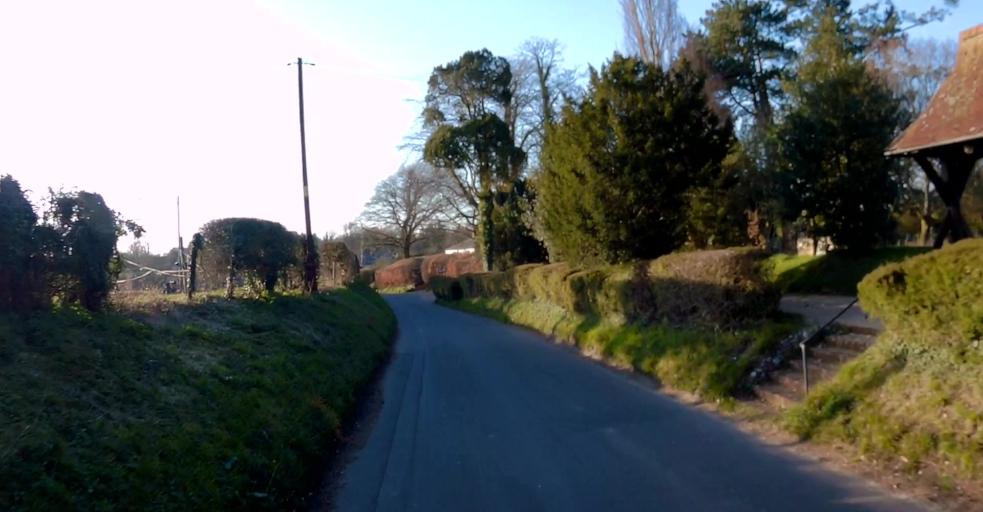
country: GB
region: England
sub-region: Hampshire
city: Basingstoke
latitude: 51.2369
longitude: -1.0951
